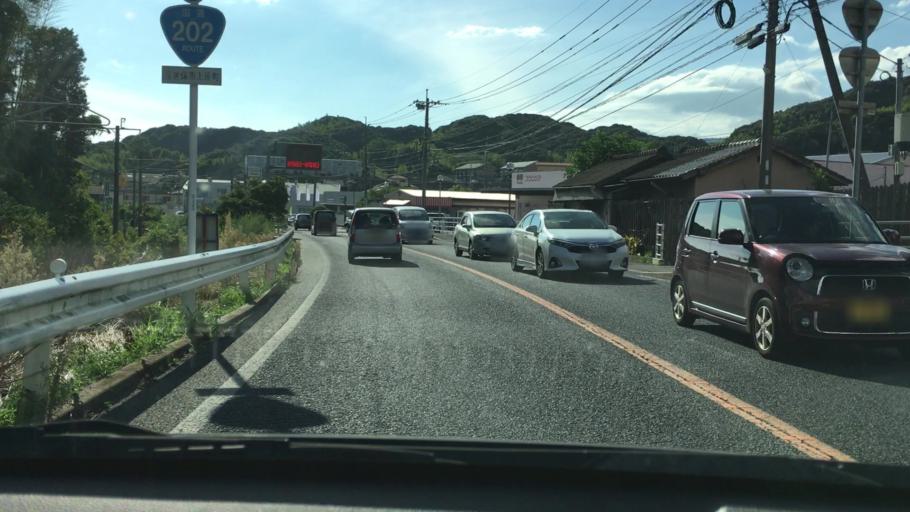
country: JP
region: Nagasaki
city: Sasebo
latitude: 33.1450
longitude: 129.8077
